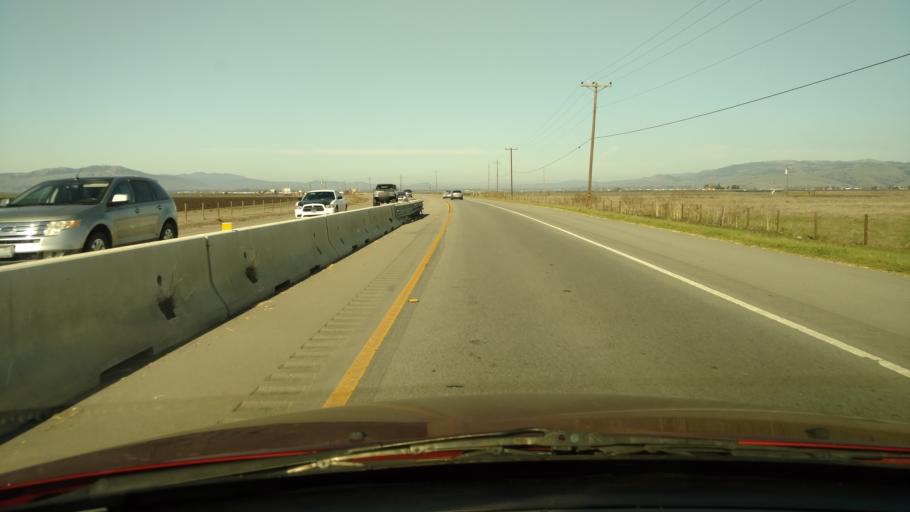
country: US
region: California
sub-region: San Benito County
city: Hollister
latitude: 36.9168
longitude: -121.4480
